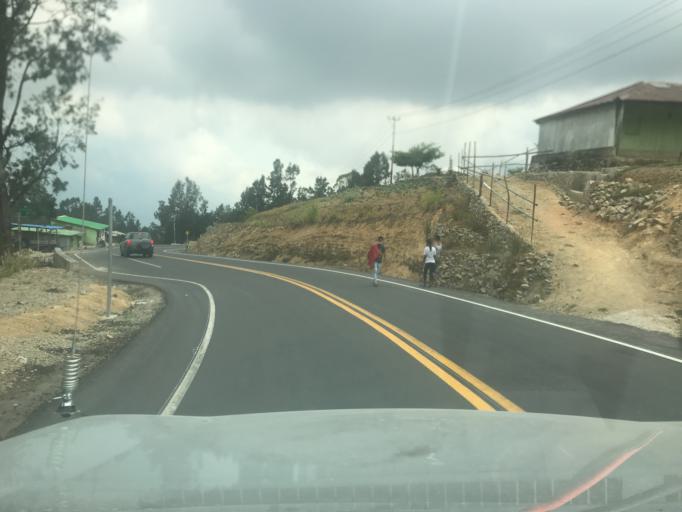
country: TL
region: Manufahi
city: Same
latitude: -8.8843
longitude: 125.6048
